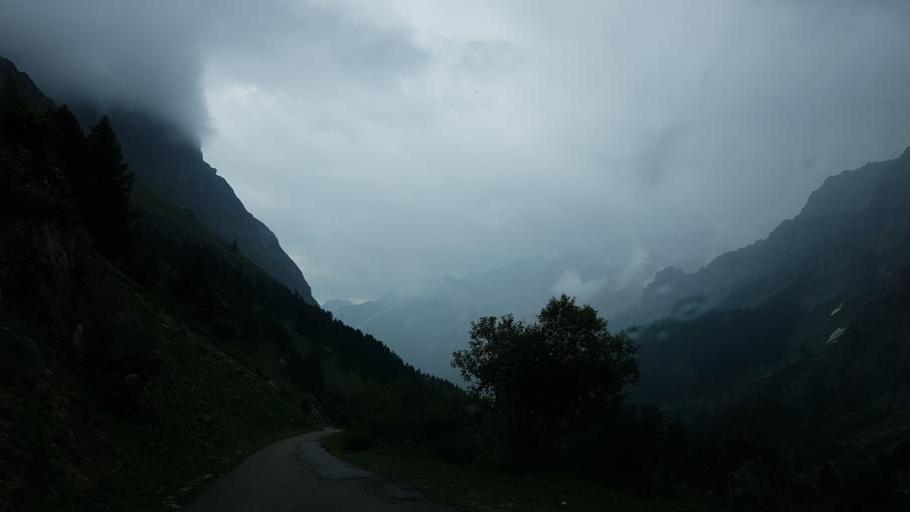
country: IT
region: Piedmont
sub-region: Provincia di Cuneo
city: Acceglio
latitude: 44.5182
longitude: 6.9078
